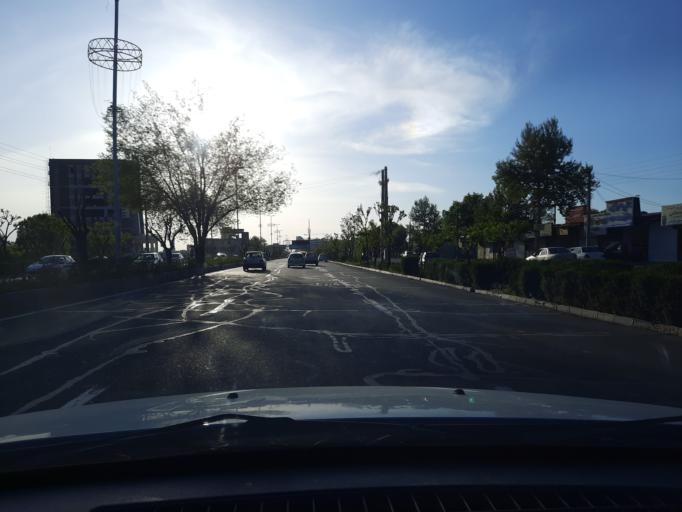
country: IR
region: Qazvin
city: Qazvin
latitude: 36.2641
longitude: 50.0342
